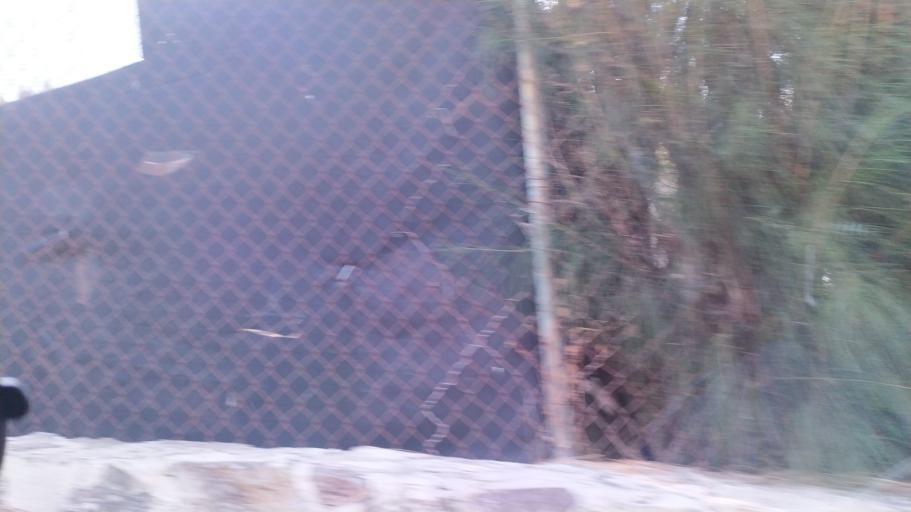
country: MX
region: Jalisco
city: Zapopan2
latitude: 20.6937
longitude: -103.4455
